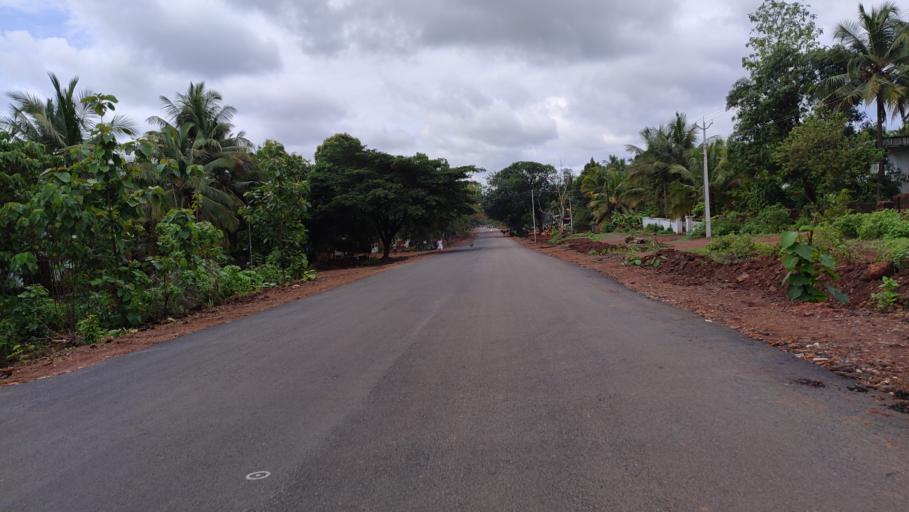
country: IN
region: Kerala
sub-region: Kasaragod District
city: Kasaragod
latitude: 12.5390
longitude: 75.0714
